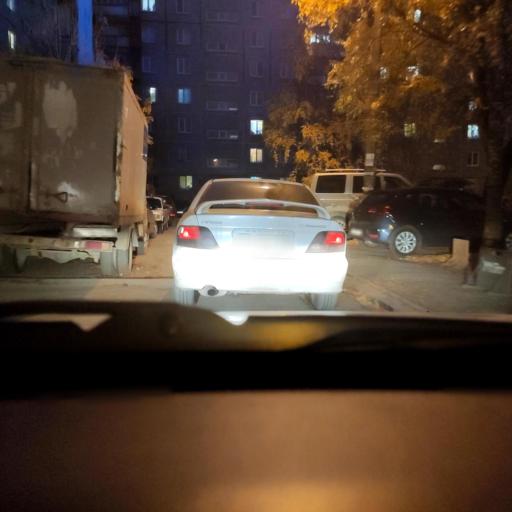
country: RU
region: Perm
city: Kondratovo
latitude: 57.9948
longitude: 56.1558
